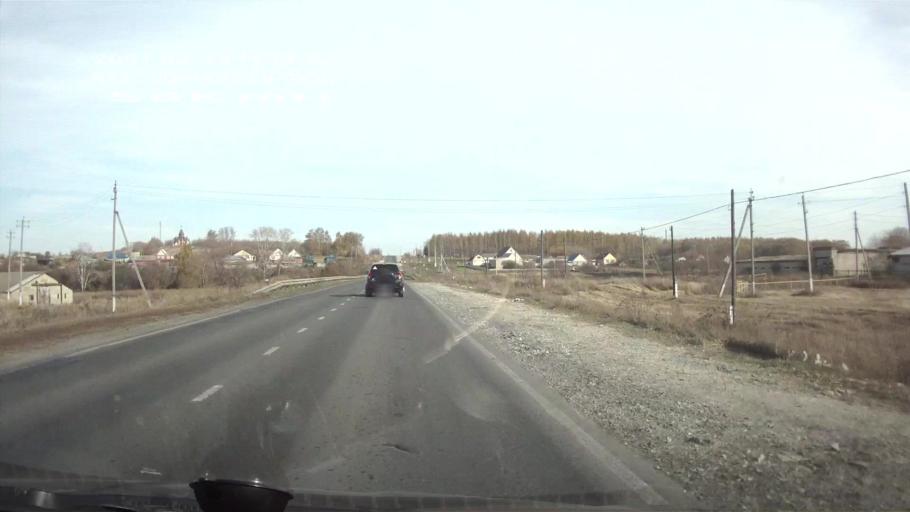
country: RU
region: Mordoviya
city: Atyashevo
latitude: 54.5609
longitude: 45.9773
